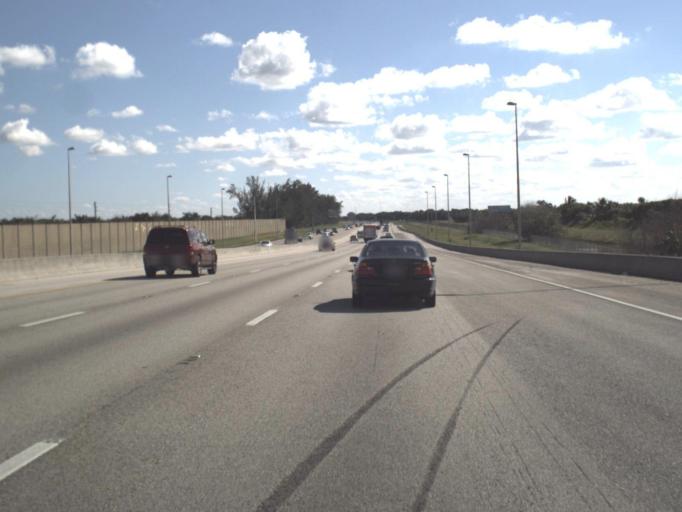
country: US
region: Florida
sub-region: Palm Beach County
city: Villages of Oriole
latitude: 26.4506
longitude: -80.1746
